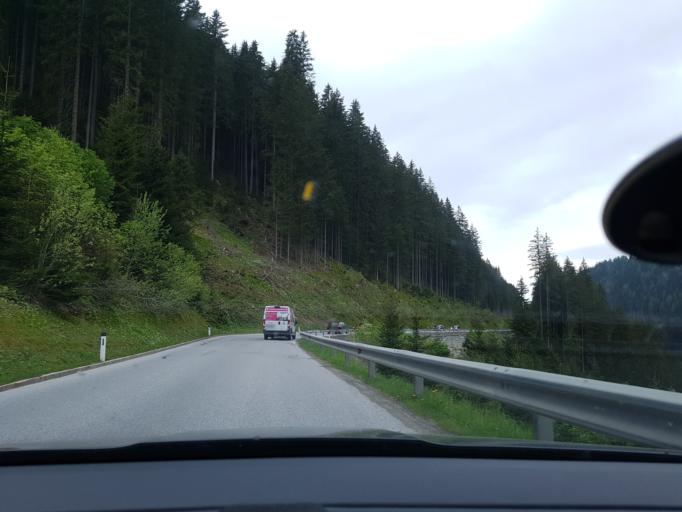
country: AT
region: Tyrol
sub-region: Politischer Bezirk Schwaz
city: Gerlos
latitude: 47.2063
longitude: 11.9763
